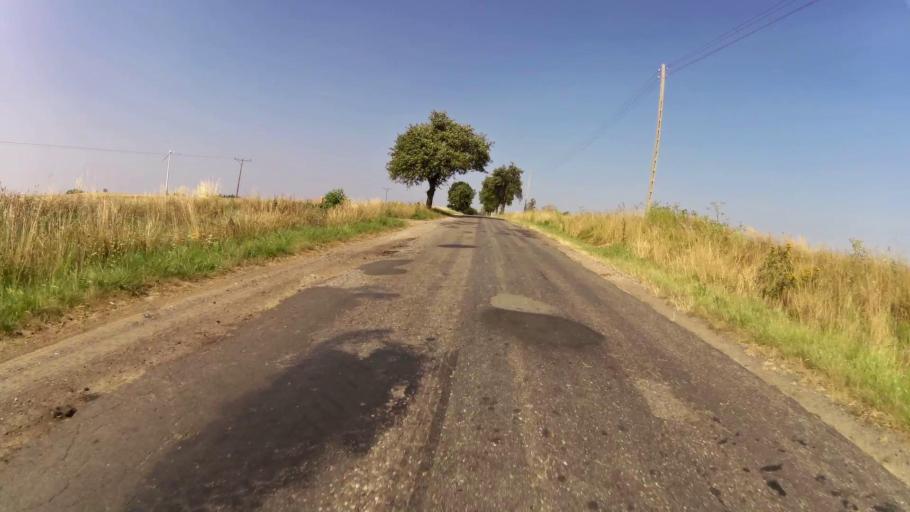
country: PL
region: West Pomeranian Voivodeship
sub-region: Powiat walecki
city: Walcz
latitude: 53.2177
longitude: 16.4740
